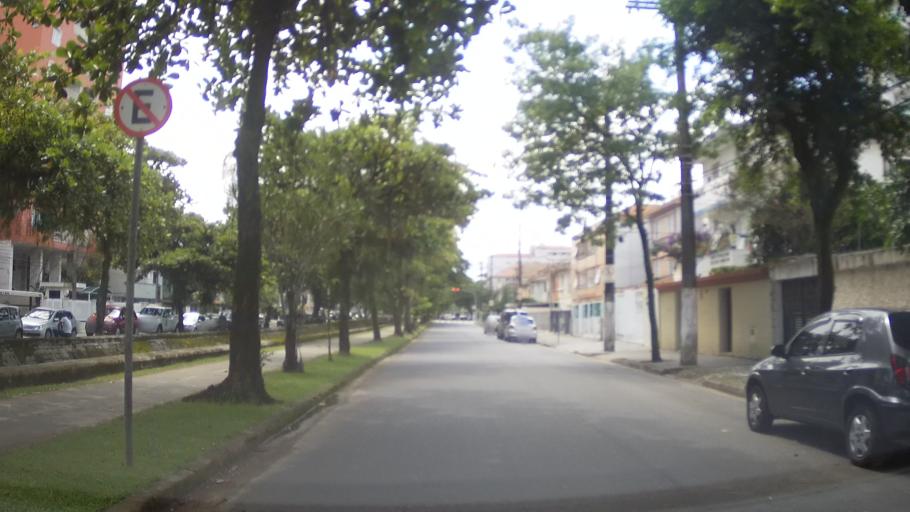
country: BR
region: Sao Paulo
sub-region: Santos
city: Santos
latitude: -23.9794
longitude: -46.3033
